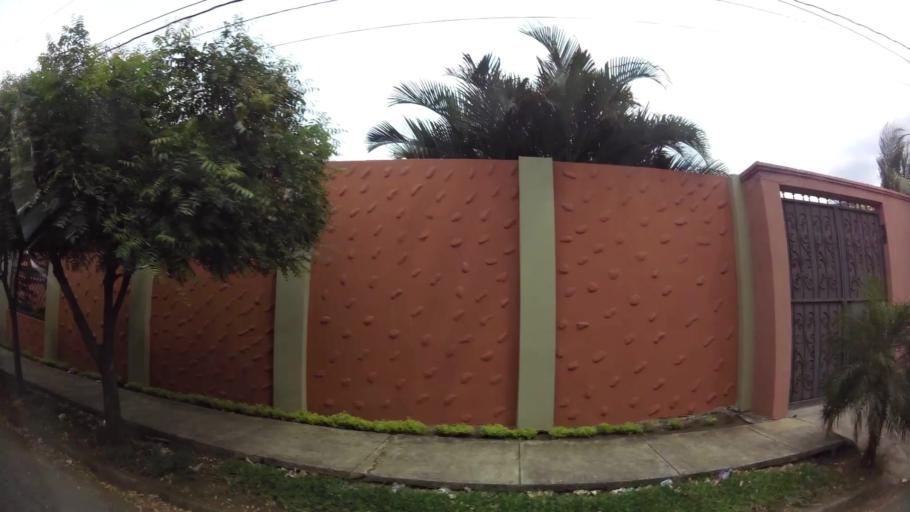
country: NI
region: Managua
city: Managua
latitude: 12.1067
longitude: -86.2434
